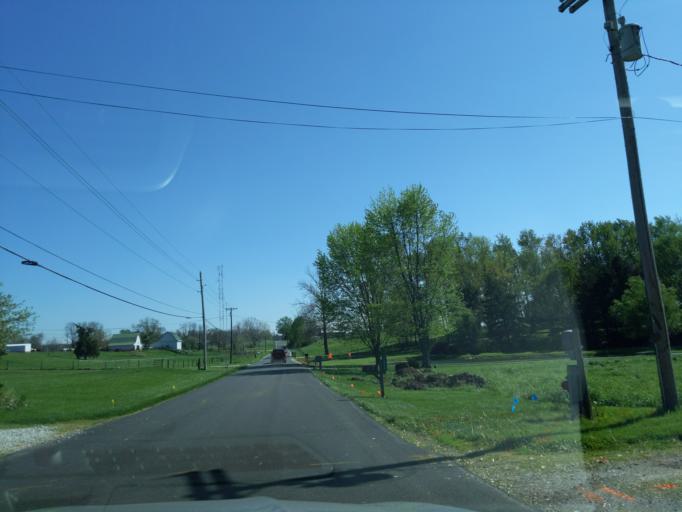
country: US
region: Indiana
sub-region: Decatur County
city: Greensburg
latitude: 39.3270
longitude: -85.4889
